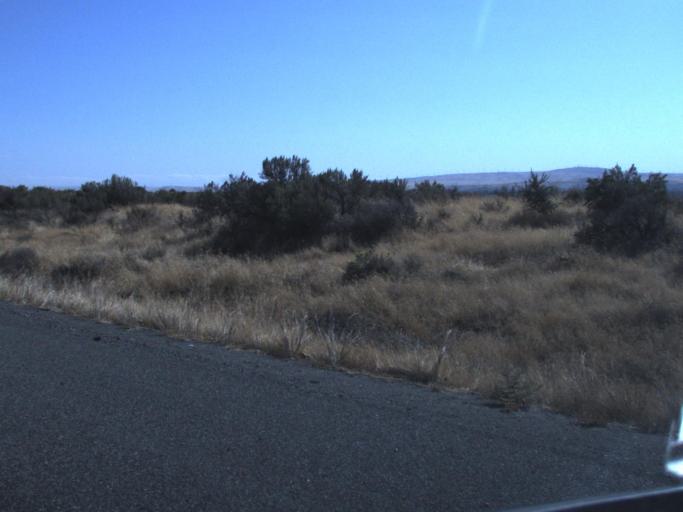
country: US
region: Washington
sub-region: Franklin County
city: West Pasco
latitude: 46.2684
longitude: -119.1918
